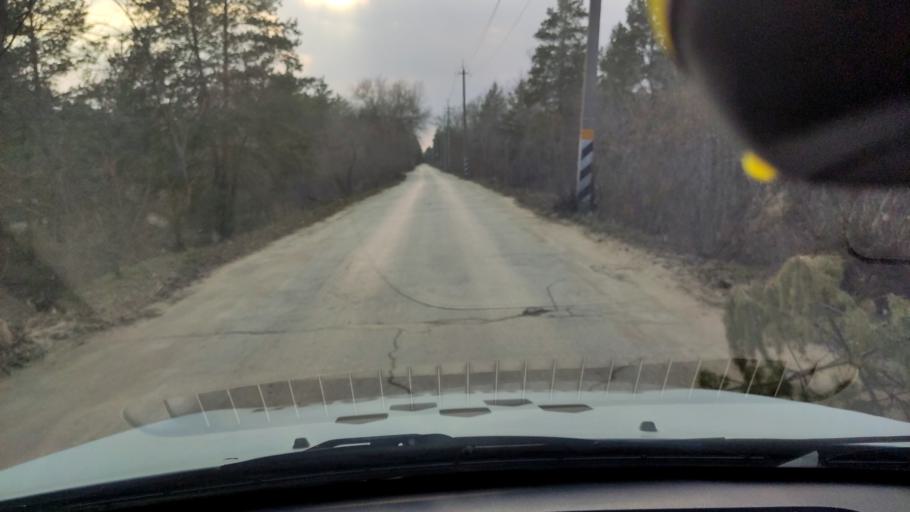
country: RU
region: Samara
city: Zhigulevsk
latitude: 53.4581
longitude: 49.6064
